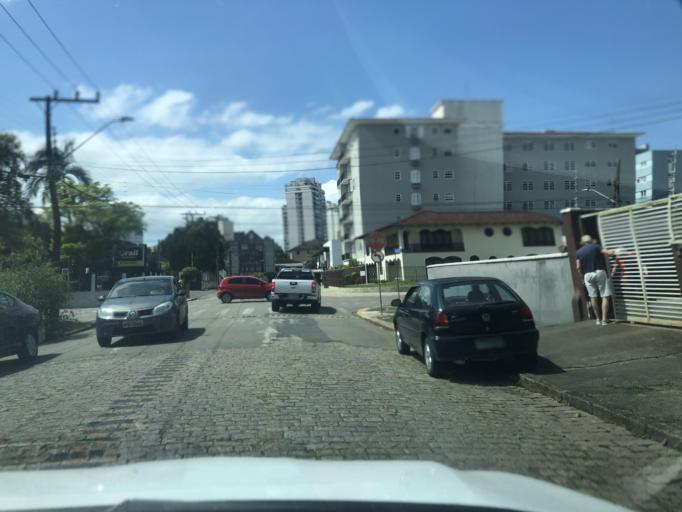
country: BR
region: Santa Catarina
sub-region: Joinville
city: Joinville
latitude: -26.3118
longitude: -48.8477
